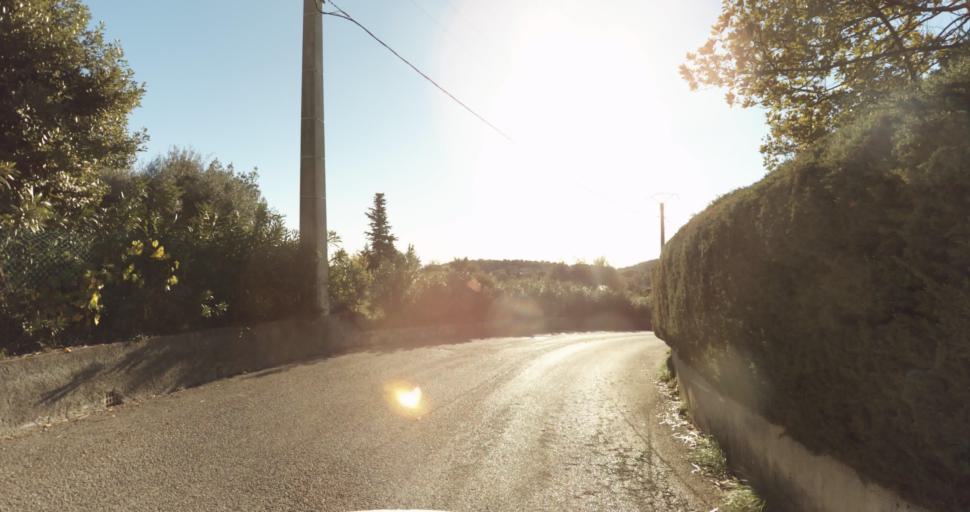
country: FR
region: Provence-Alpes-Cote d'Azur
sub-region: Departement des Alpes-Maritimes
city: Vence
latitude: 43.7251
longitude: 7.0856
